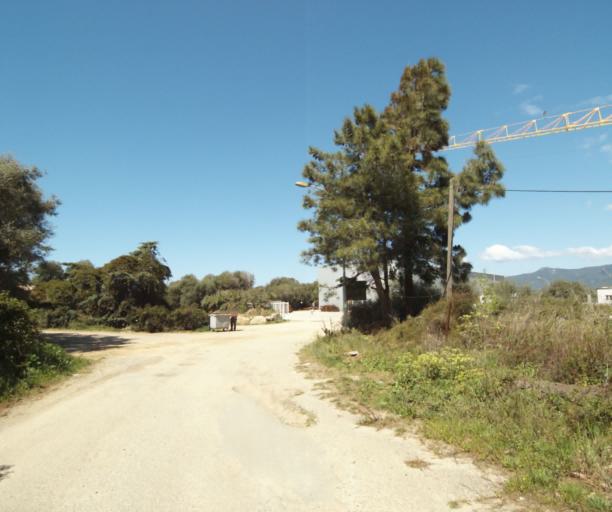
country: FR
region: Corsica
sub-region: Departement de la Corse-du-Sud
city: Propriano
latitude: 41.6535
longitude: 8.8996
